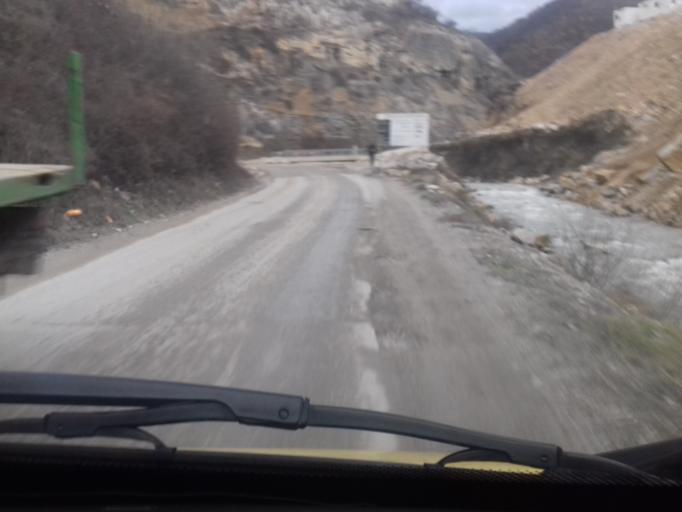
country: BA
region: Federation of Bosnia and Herzegovina
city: Zenica
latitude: 44.2120
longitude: 17.9335
